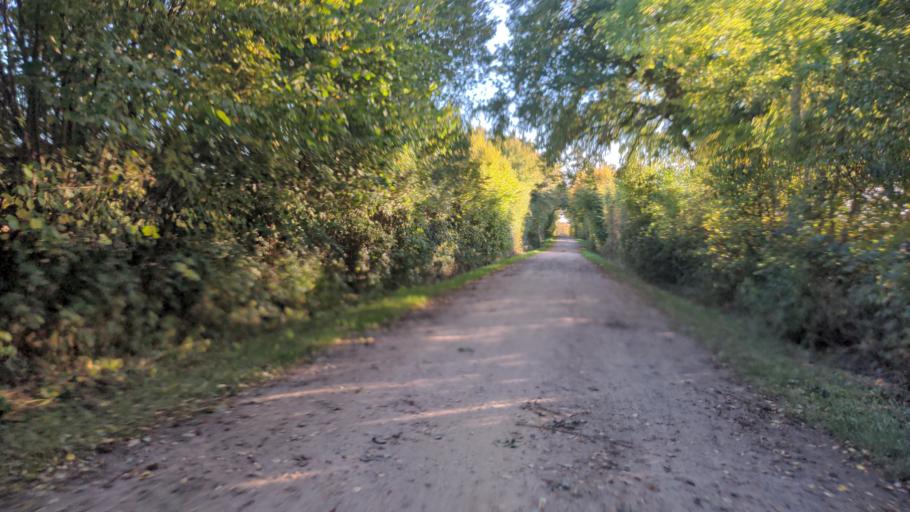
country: DE
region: Schleswig-Holstein
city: Neustadt in Holstein
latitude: 54.0957
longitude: 10.8466
